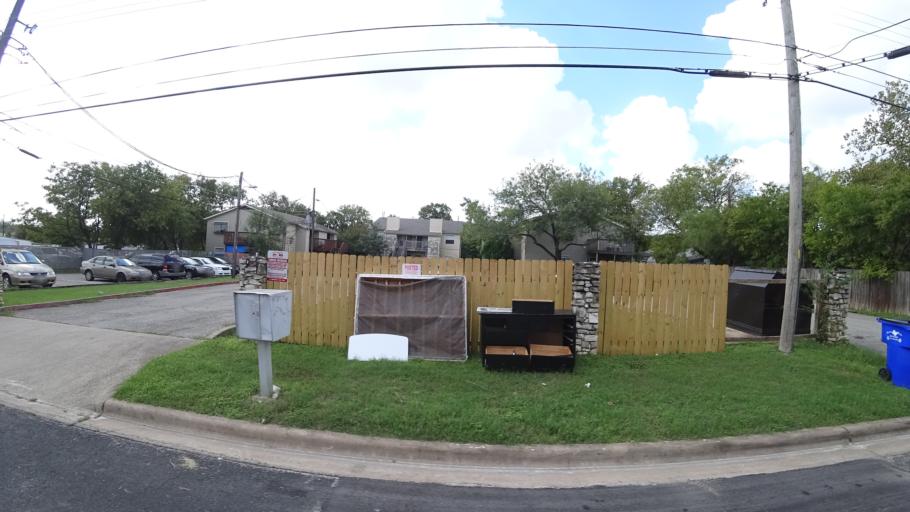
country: US
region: Texas
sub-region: Travis County
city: Austin
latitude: 30.3457
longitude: -97.7156
